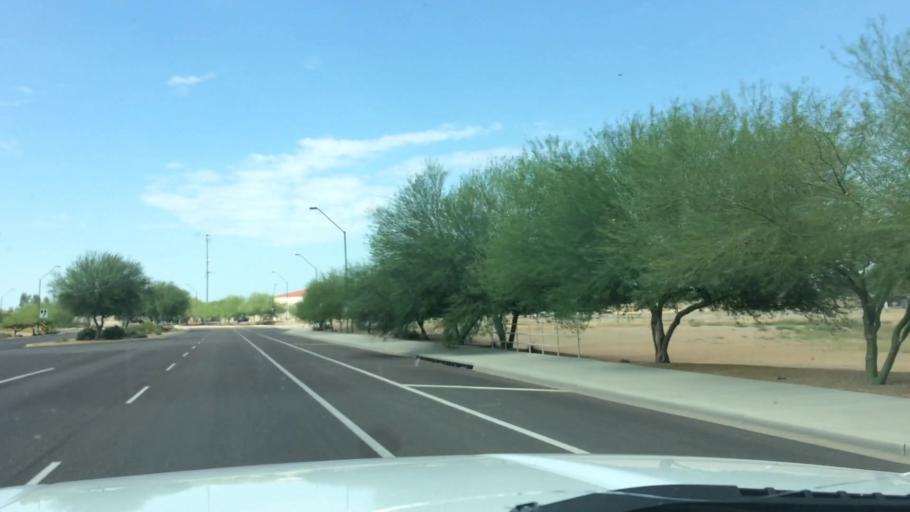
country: US
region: Arizona
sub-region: Maricopa County
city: Peoria
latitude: 33.5763
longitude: -112.2357
